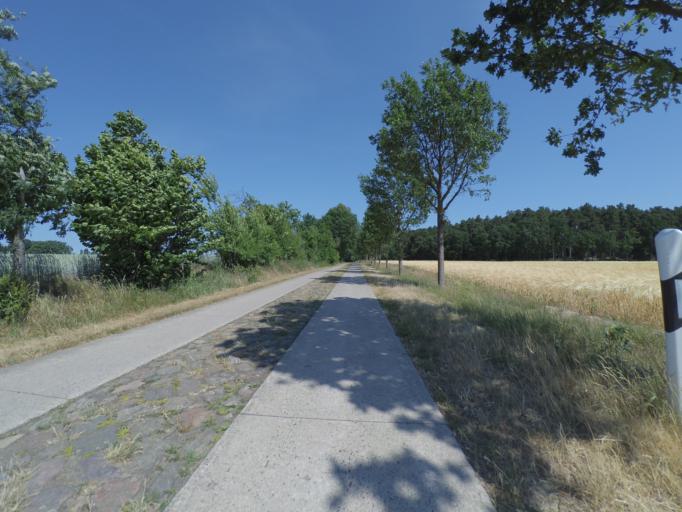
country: DE
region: Brandenburg
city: Heiligengrabe
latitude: 53.2411
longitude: 12.3150
